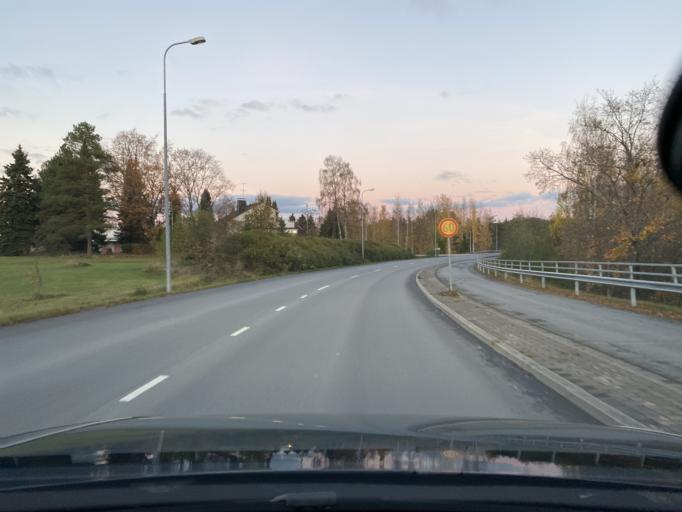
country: FI
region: Pirkanmaa
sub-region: Tampere
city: Lempaeaelae
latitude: 61.3282
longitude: 23.7617
